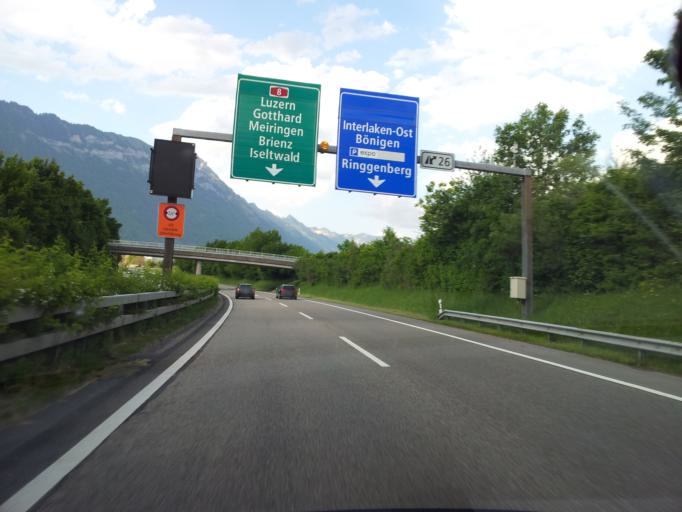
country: CH
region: Bern
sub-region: Interlaken-Oberhasli District
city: Matten
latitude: 46.6755
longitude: 7.8742
